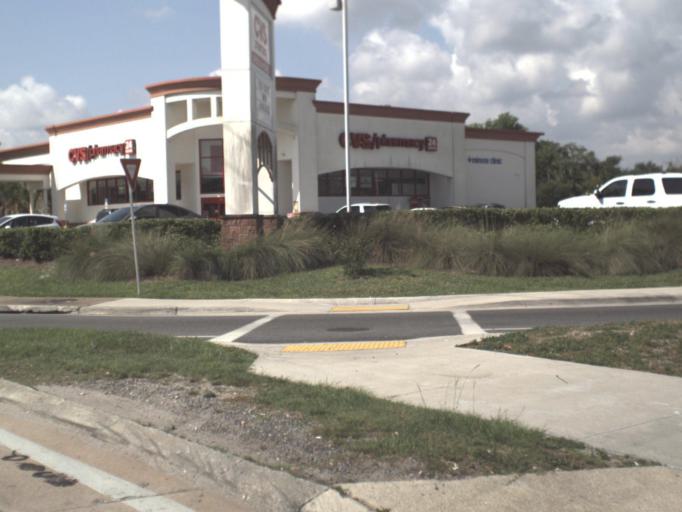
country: US
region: Florida
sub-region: Saint Johns County
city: Saint Augustine
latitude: 29.9167
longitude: -81.3247
